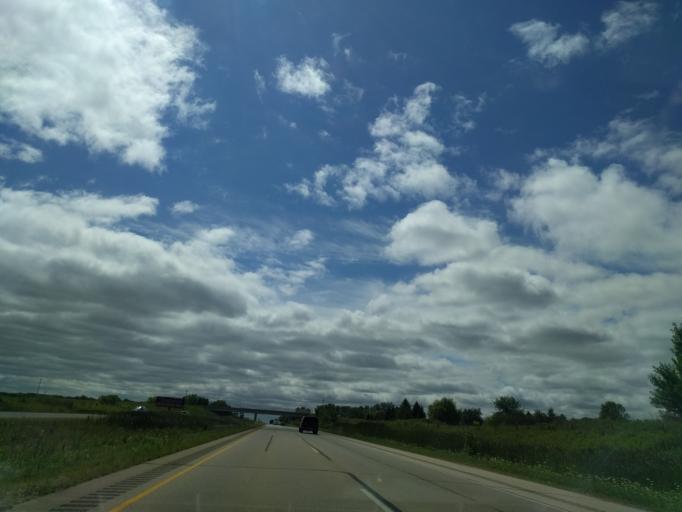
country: US
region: Wisconsin
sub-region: Brown County
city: Suamico
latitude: 44.7093
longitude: -88.0510
